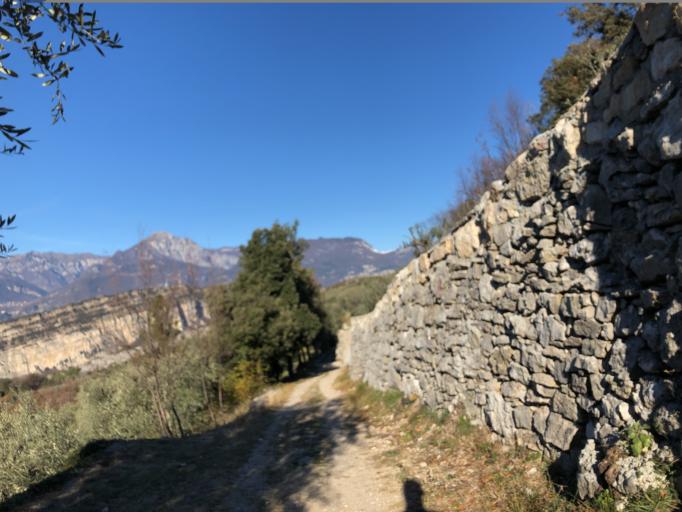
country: IT
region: Trentino-Alto Adige
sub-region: Provincia di Trento
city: Torbole sul Garda
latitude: 45.8652
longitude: 10.8853
